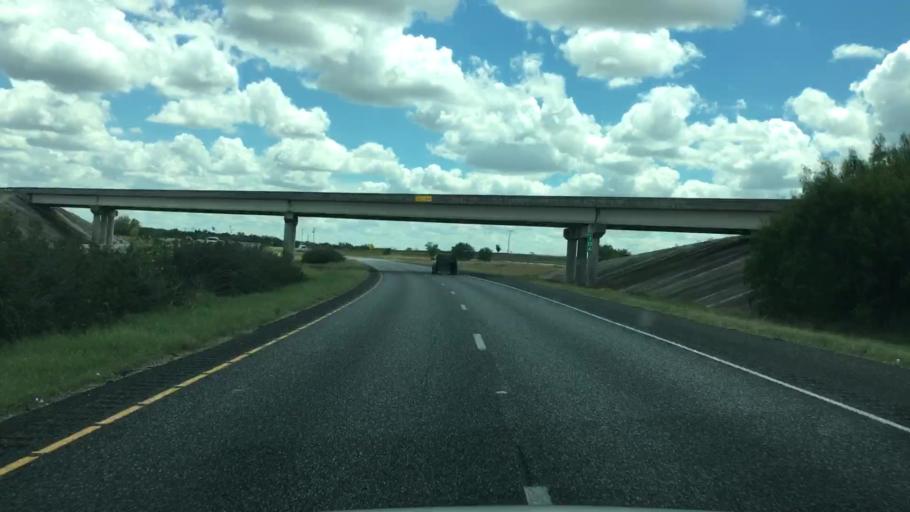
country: US
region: Texas
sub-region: Atascosa County
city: Pleasanton
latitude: 28.9107
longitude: -98.4343
